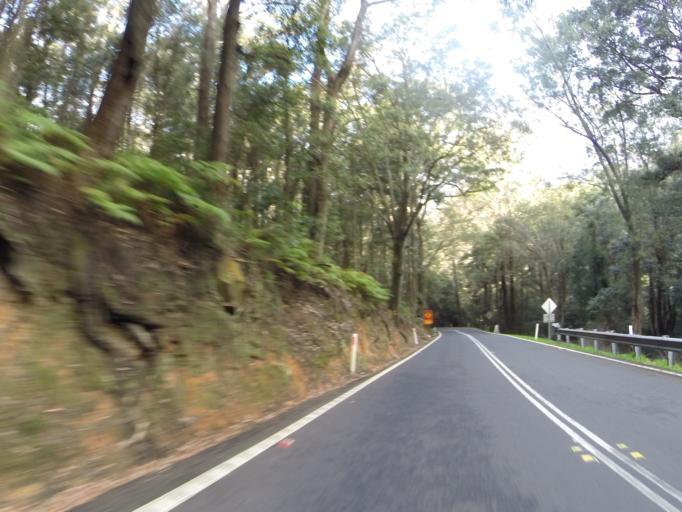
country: AU
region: New South Wales
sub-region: Shellharbour
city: Calderwood
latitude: -34.5714
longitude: 150.6743
